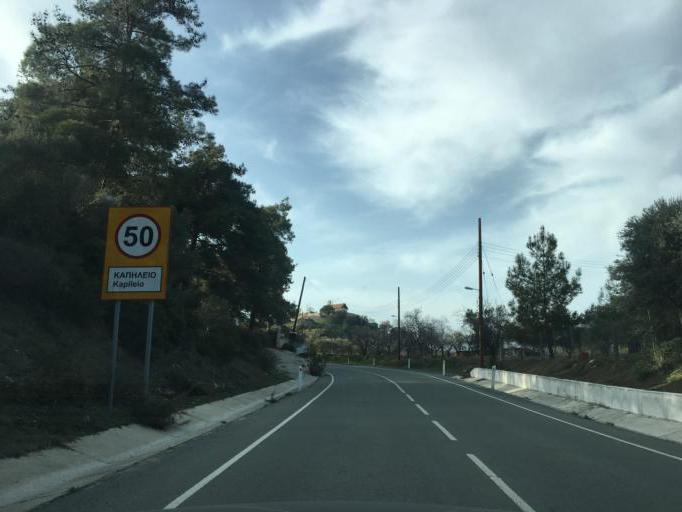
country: CY
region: Limassol
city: Pelendri
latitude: 34.8299
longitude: 32.9618
